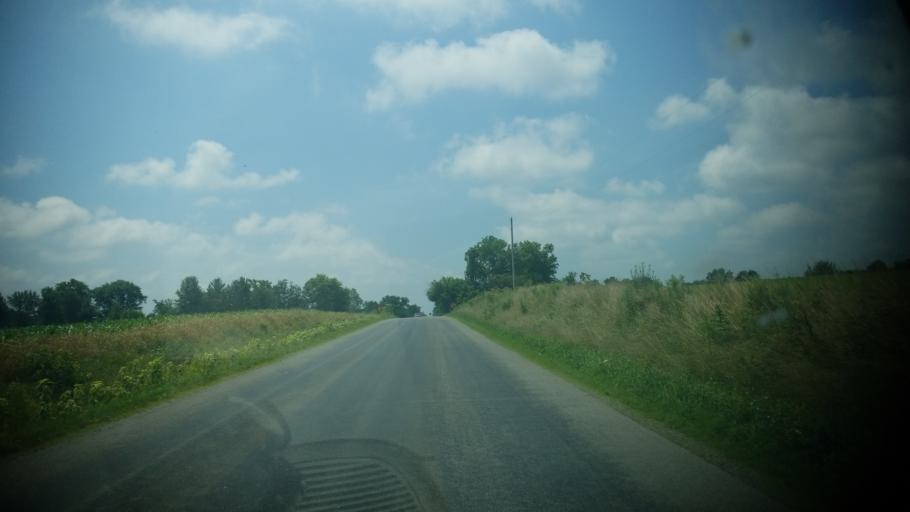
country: US
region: Illinois
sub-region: Wayne County
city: Fairfield
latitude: 38.5169
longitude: -88.3485
